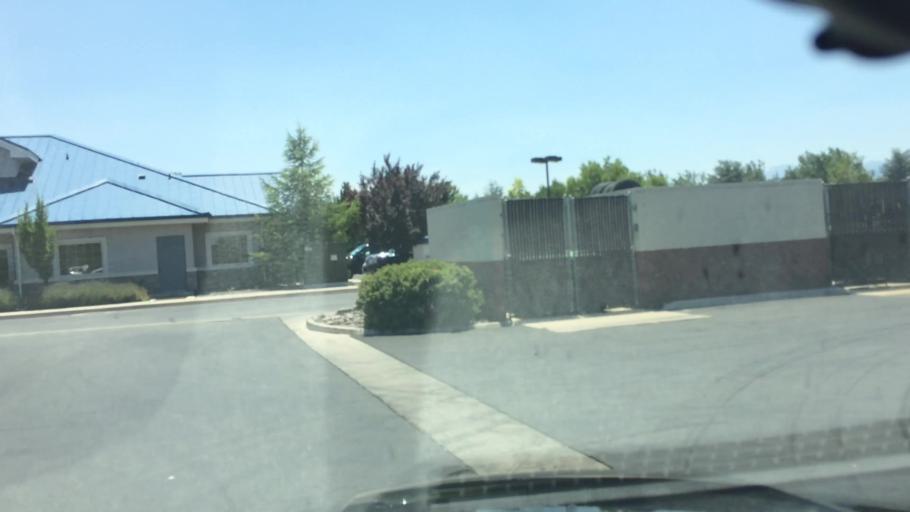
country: US
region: Nevada
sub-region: Washoe County
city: Sparks
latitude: 39.5413
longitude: -119.7174
